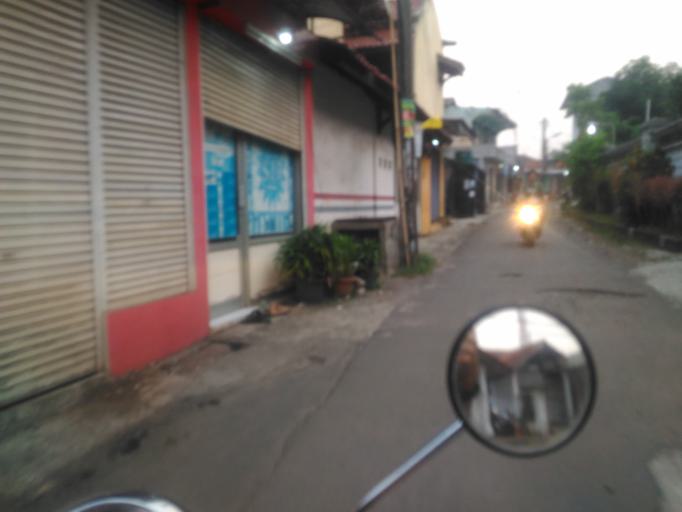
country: ID
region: West Java
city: Depok
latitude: -6.3662
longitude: 106.8375
